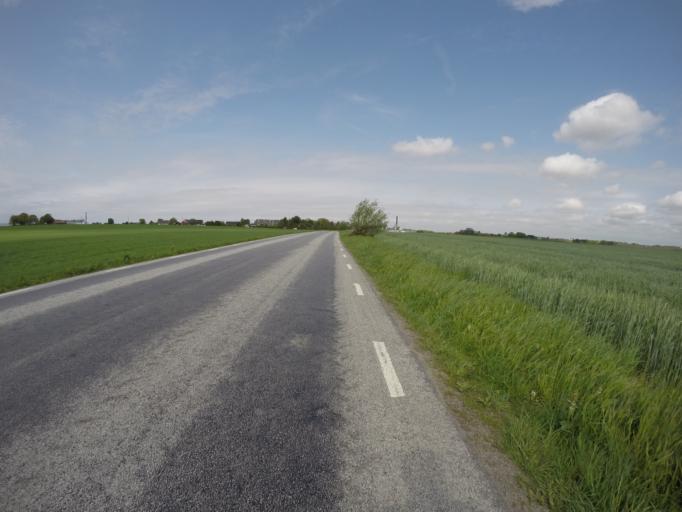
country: SE
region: Skane
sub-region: Malmo
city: Tygelsjo
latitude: 55.5270
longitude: 13.0240
